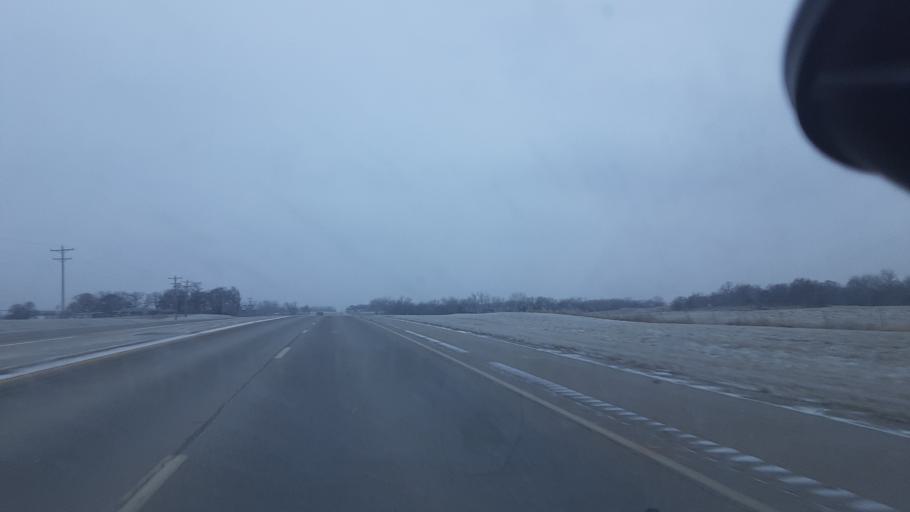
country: US
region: Oklahoma
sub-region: Payne County
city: Perkins
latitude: 35.9854
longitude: -97.0739
